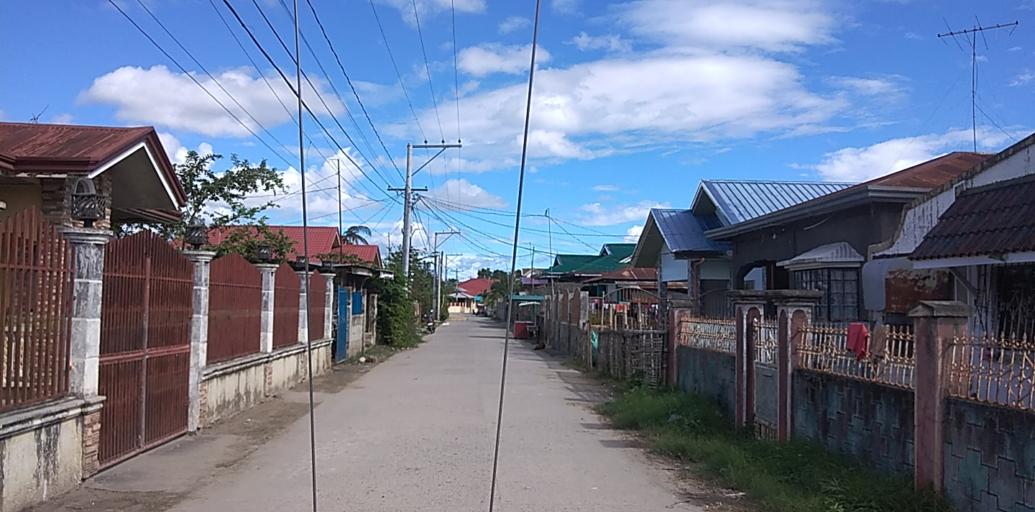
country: PH
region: Central Luzon
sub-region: Province of Pampanga
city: Candating
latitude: 15.1370
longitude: 120.8016
